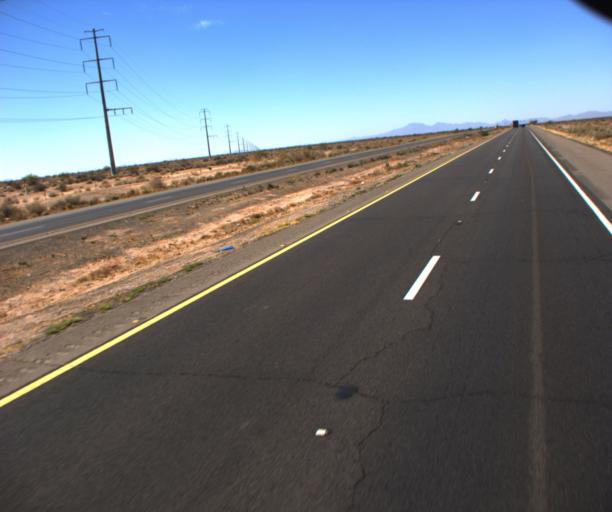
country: US
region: Arizona
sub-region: Pinal County
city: Maricopa
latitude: 33.1316
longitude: -112.0135
